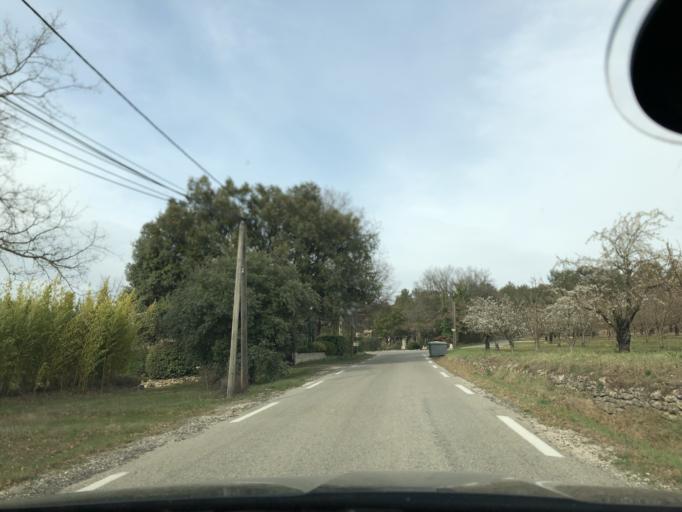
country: FR
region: Provence-Alpes-Cote d'Azur
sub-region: Departement du Vaucluse
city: Goult
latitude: 43.8457
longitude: 5.2259
